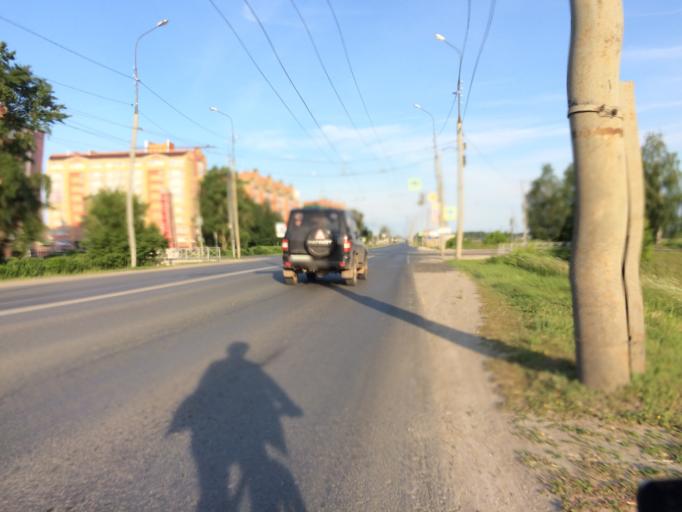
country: RU
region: Mariy-El
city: Medvedevo
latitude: 56.6395
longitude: 47.8039
